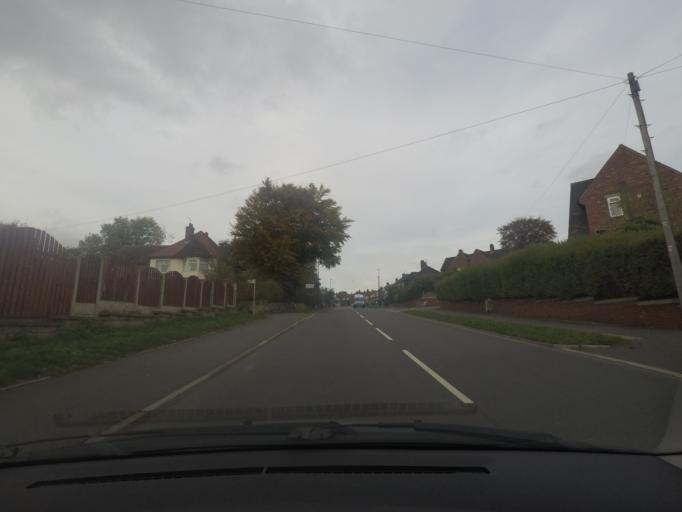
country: GB
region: England
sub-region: Sheffield
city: Oughtibridge
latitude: 53.4262
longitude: -1.5003
